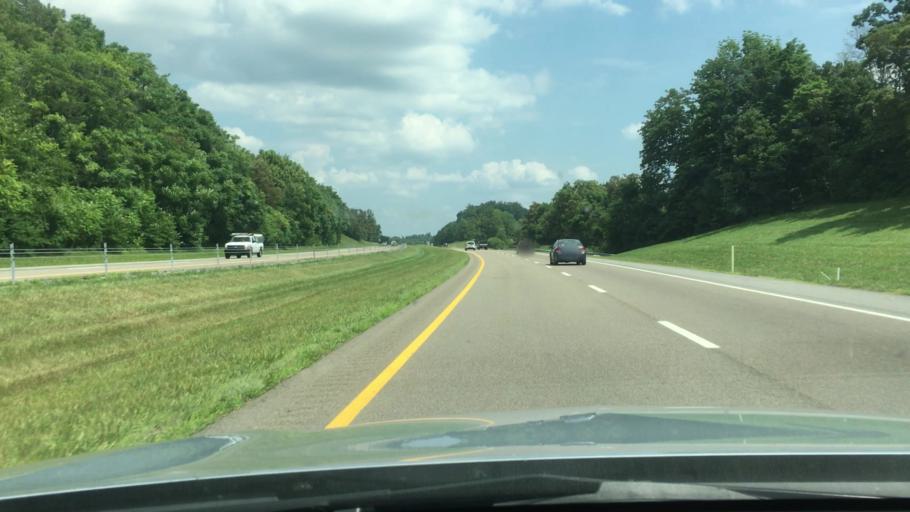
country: US
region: Tennessee
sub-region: Carter County
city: Pine Crest
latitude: 36.2550
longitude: -82.3231
